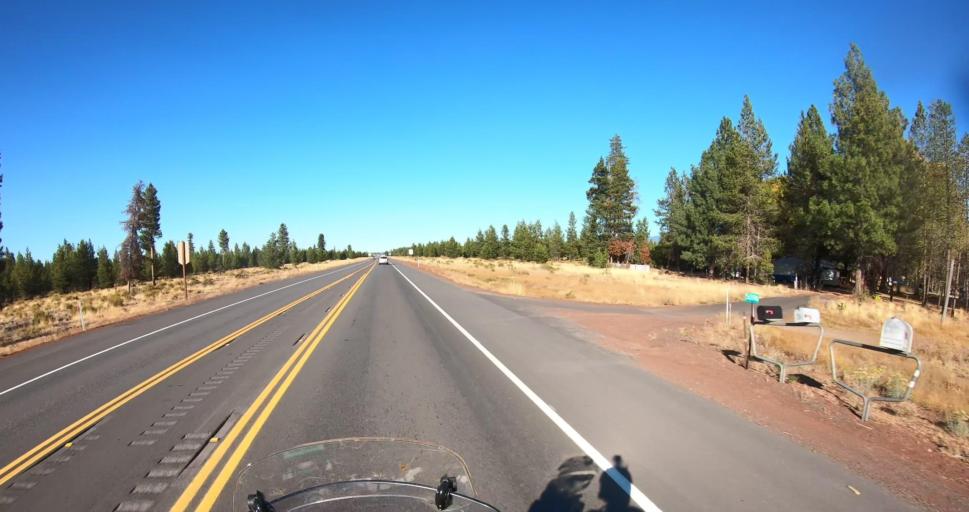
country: US
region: Oregon
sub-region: Deschutes County
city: La Pine
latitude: 43.6495
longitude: -121.5190
